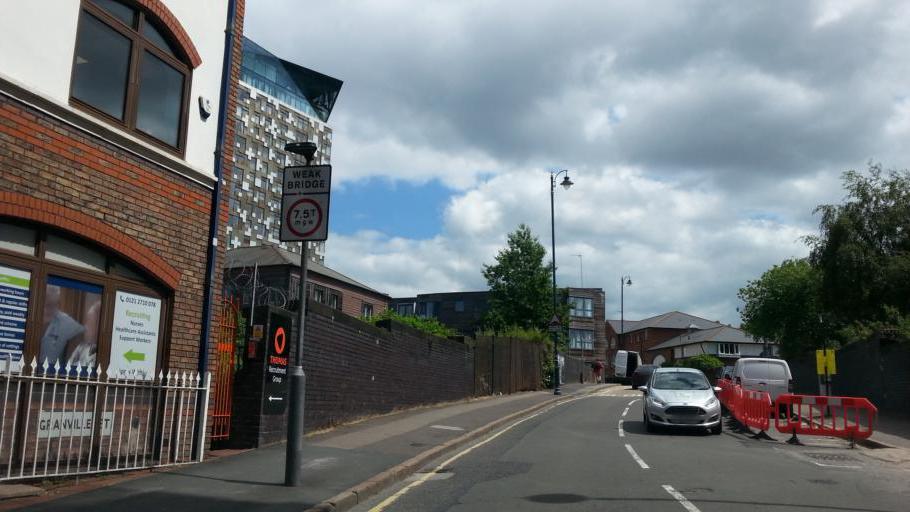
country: GB
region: England
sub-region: City and Borough of Birmingham
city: Birmingham
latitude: 52.4751
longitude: -1.9092
